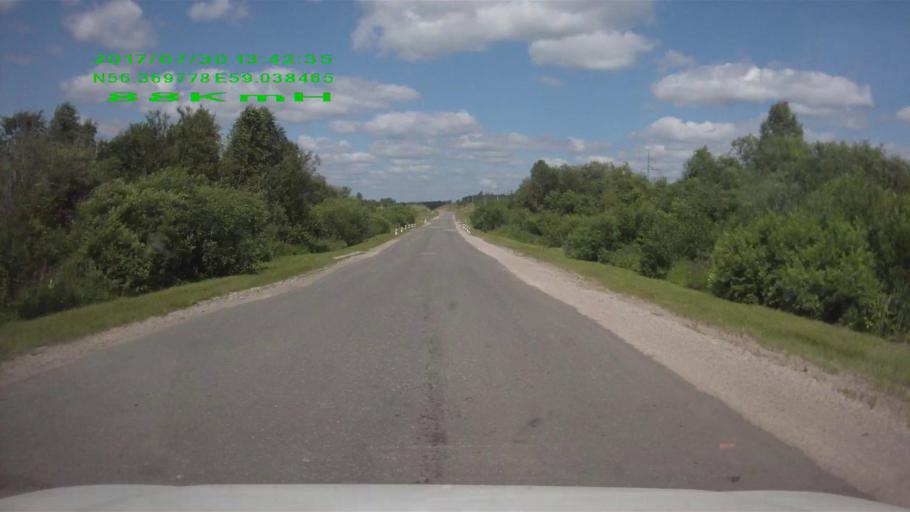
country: RU
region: Sverdlovsk
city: Mikhaylovsk
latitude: 56.3701
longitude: 59.0385
